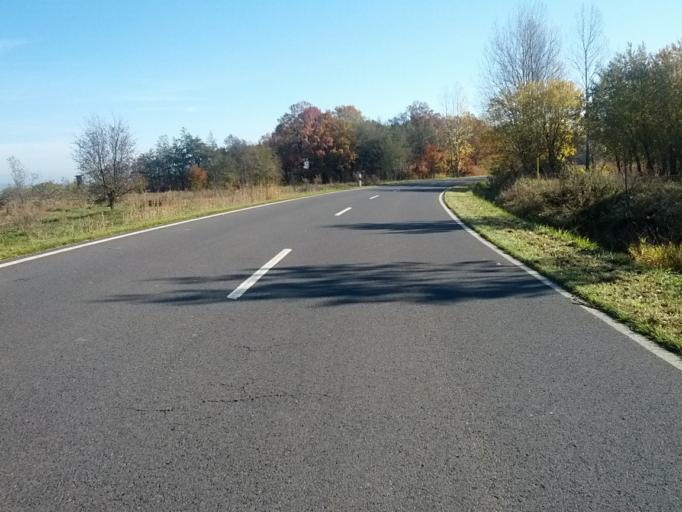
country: DE
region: Thuringia
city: Haina
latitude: 50.9984
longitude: 10.4674
